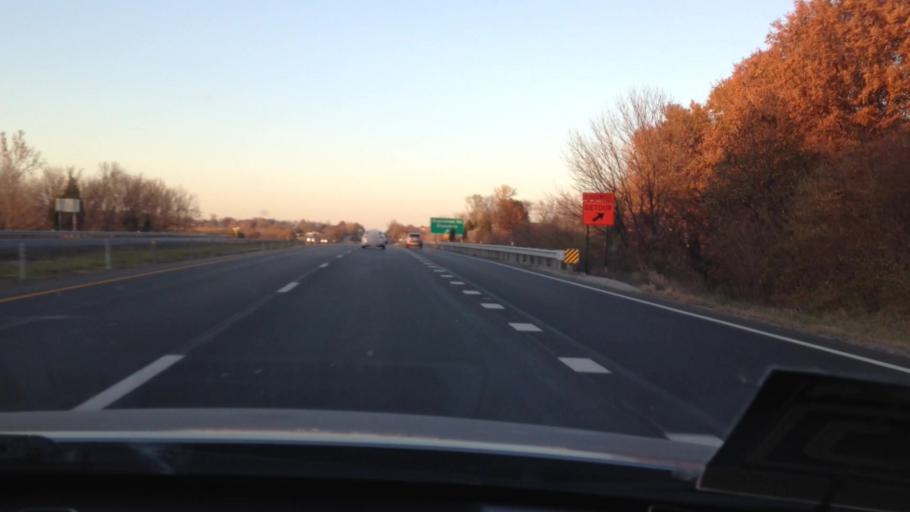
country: US
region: Missouri
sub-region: Platte County
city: Riverside
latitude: 39.1909
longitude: -94.5901
